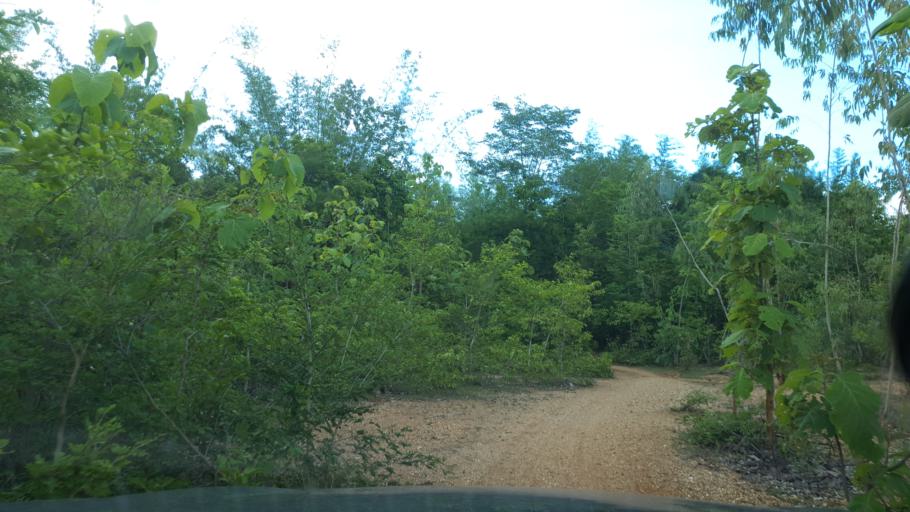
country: TH
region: Lampang
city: Sop Prap
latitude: 17.8878
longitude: 99.2889
